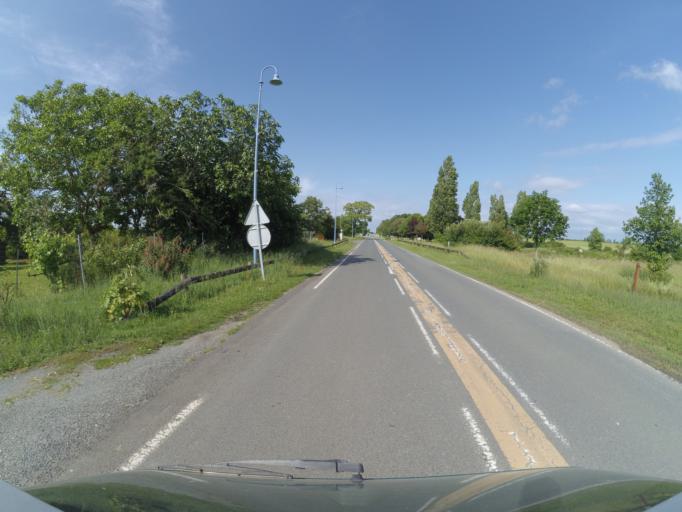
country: FR
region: Poitou-Charentes
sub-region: Departement de la Charente-Maritime
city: Andilly
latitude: 46.2457
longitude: -1.0626
